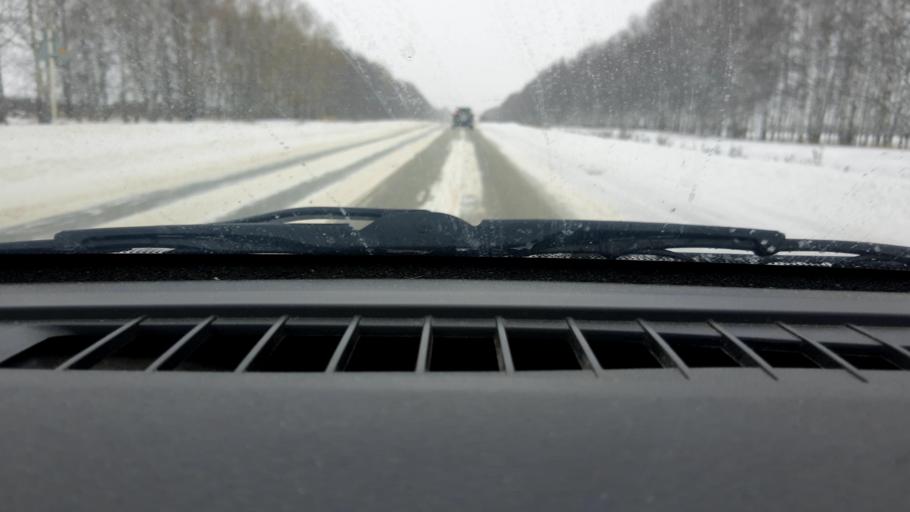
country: RU
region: Vladimir
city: Vorsha
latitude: 56.1104
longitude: 40.0716
